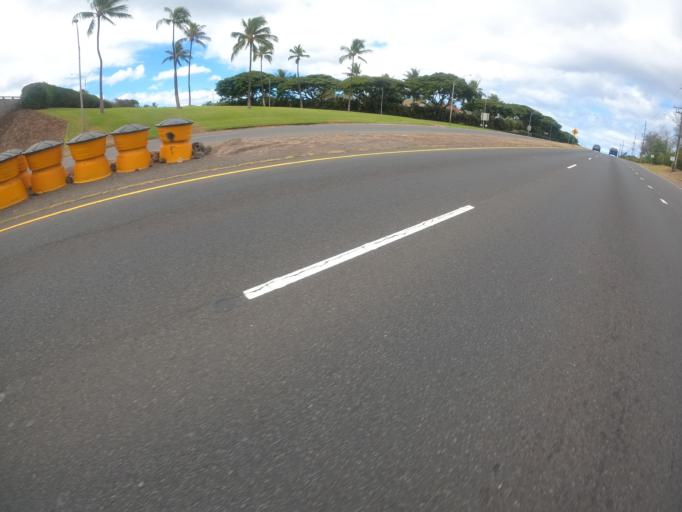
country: US
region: Hawaii
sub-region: Honolulu County
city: Makakilo
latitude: 21.3466
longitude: -158.1242
